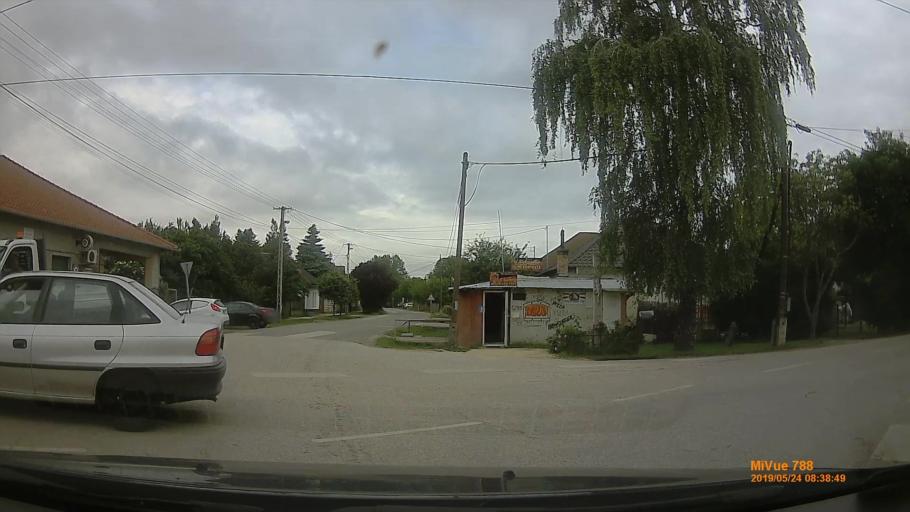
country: HU
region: Pest
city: Ullo
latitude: 47.3894
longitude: 19.3525
